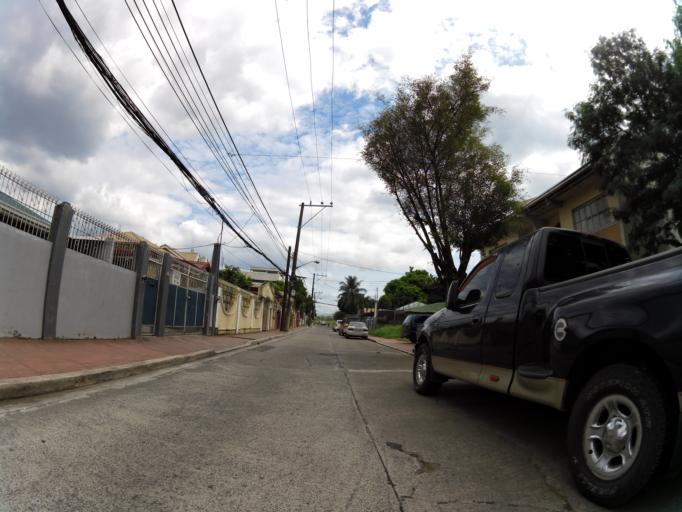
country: PH
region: Metro Manila
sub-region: Marikina
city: Calumpang
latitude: 14.6341
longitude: 121.1003
